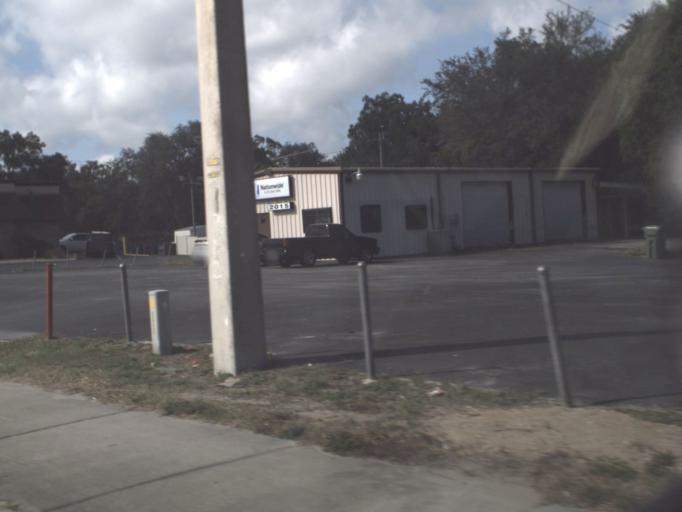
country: US
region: Florida
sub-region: Lake County
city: Fruitland Park
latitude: 28.8393
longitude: -81.8931
